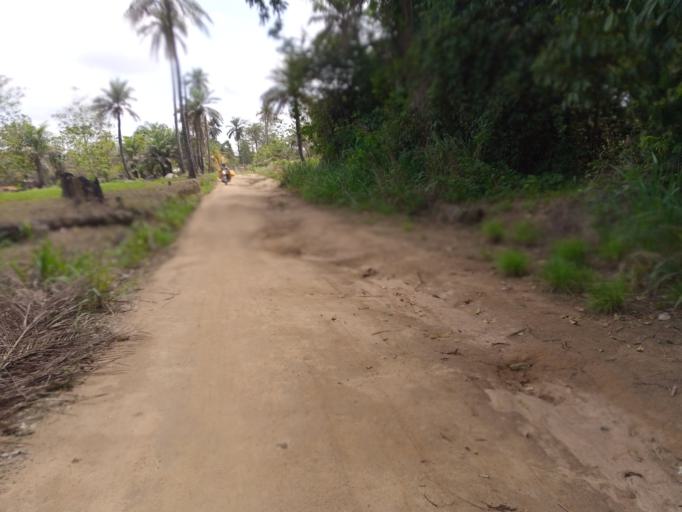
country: SL
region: Western Area
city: Waterloo
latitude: 8.3217
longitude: -13.0113
